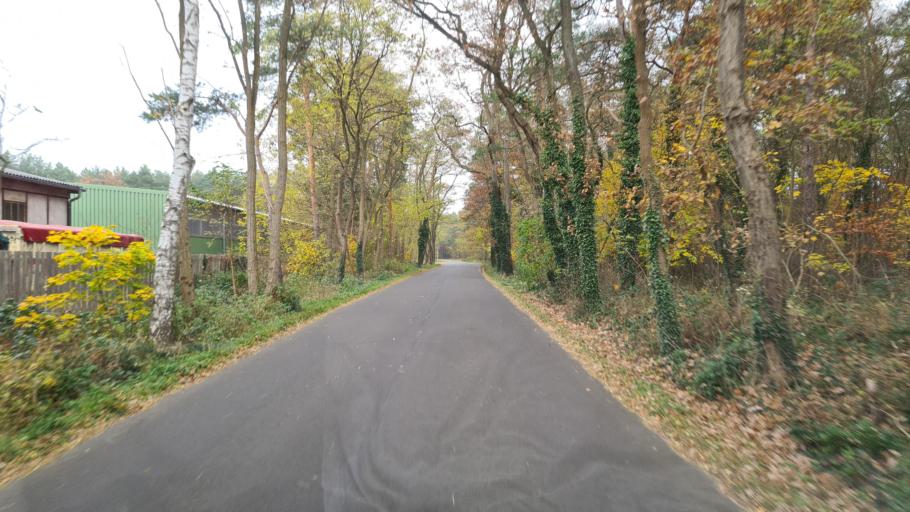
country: DE
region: Brandenburg
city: Gross Kreutz
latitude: 52.3414
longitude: 12.7337
